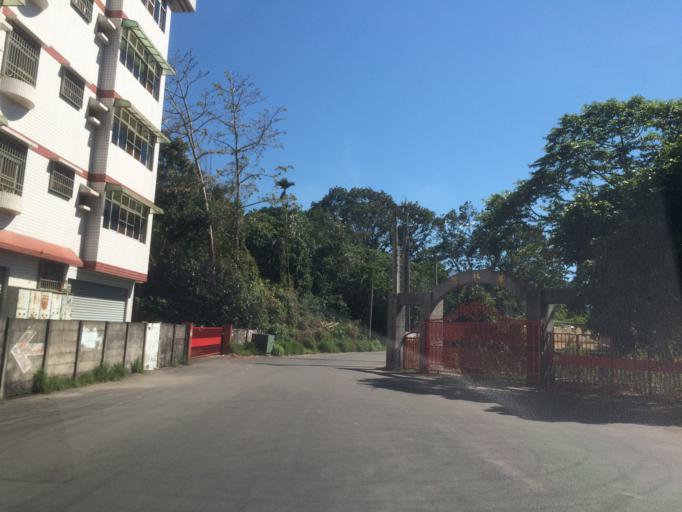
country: TW
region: Taiwan
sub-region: Yunlin
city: Douliu
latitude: 23.7065
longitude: 120.6086
